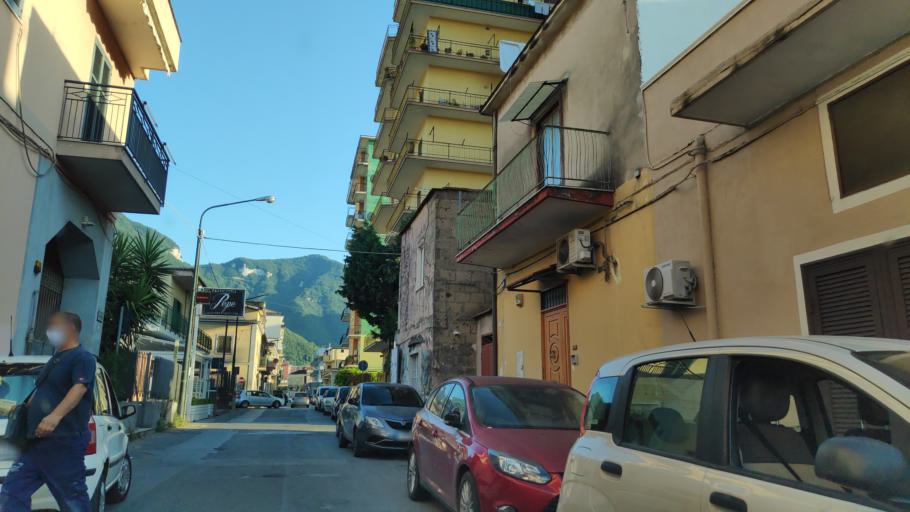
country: IT
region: Campania
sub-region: Provincia di Salerno
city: Pagani
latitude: 40.7497
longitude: 14.6149
